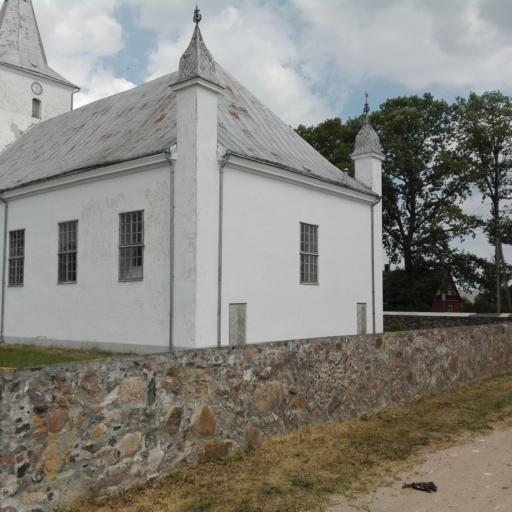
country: LT
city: Obeliai
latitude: 56.1185
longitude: 25.0035
